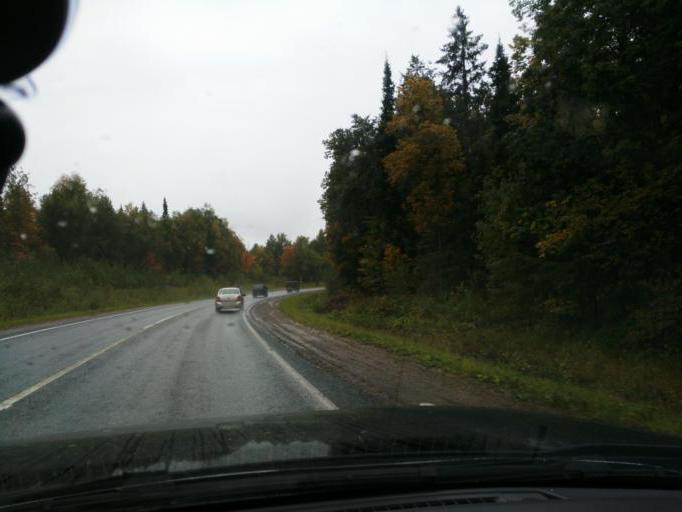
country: RU
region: Perm
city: Yugo-Kamskiy
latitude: 57.5976
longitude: 55.6548
